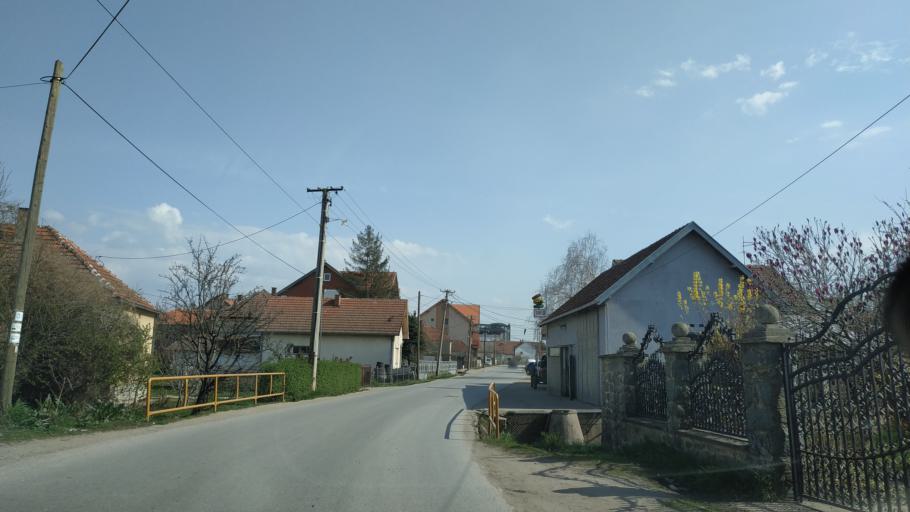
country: RS
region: Central Serbia
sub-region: Nisavski Okrug
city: Aleksinac
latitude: 43.5111
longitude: 21.6911
